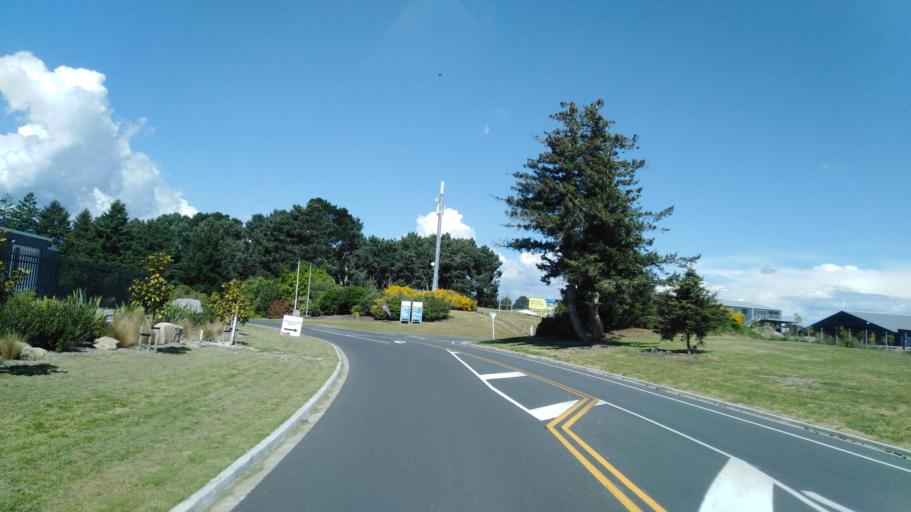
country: NZ
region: Waikato
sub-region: Taupo District
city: Taupo
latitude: -38.7397
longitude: 176.0761
